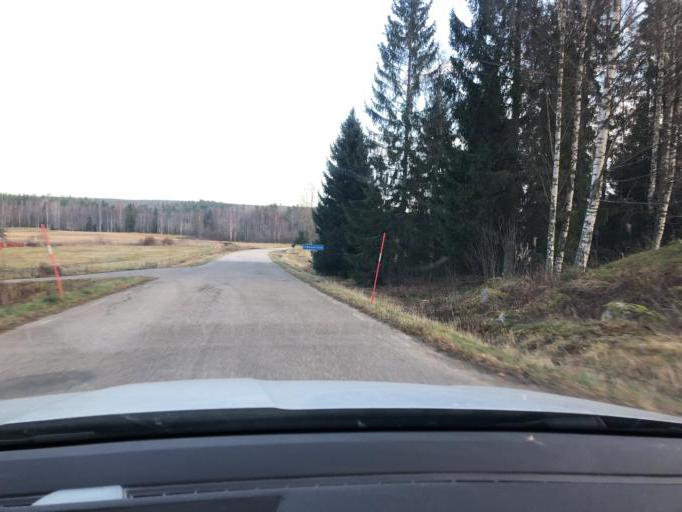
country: SE
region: Gaevleborg
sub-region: Hudiksvalls Kommun
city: Sorforsa
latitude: 61.7125
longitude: 16.9406
